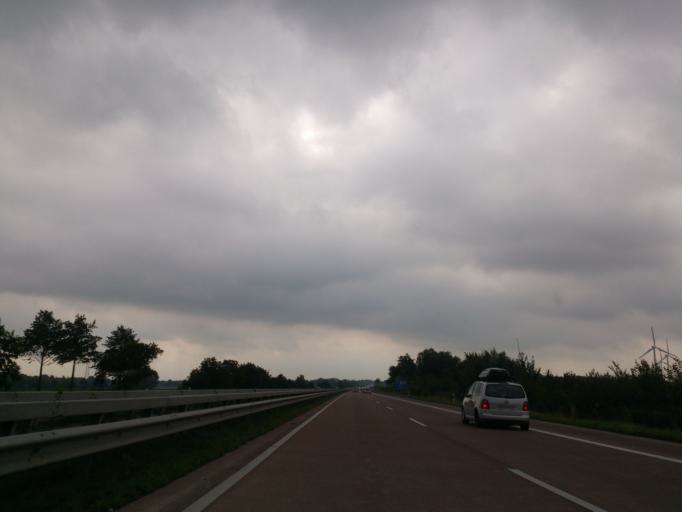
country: DE
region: Schleswig-Holstein
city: Hohenfelde
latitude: 53.8380
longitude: 9.6125
